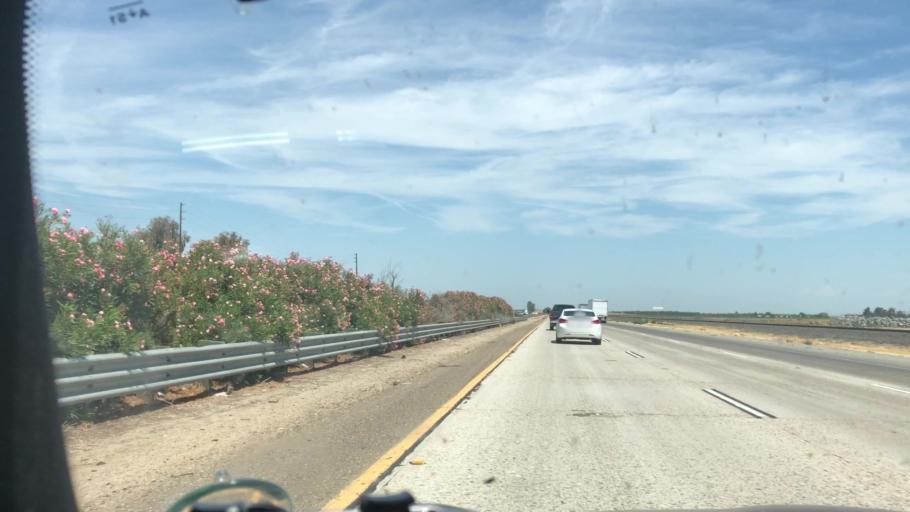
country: US
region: California
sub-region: Kern County
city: McFarland
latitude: 35.6293
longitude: -119.2158
